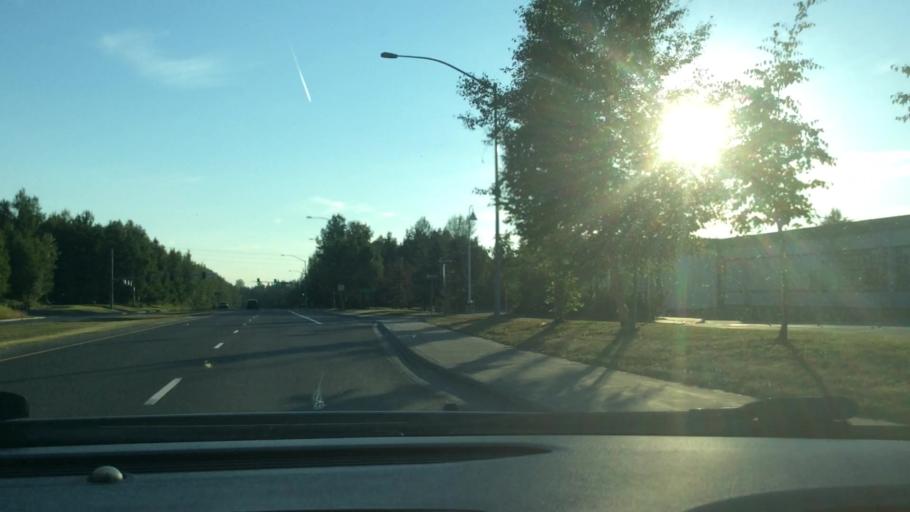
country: US
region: Alaska
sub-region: Anchorage Municipality
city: Anchorage
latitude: 61.1990
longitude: -149.8049
